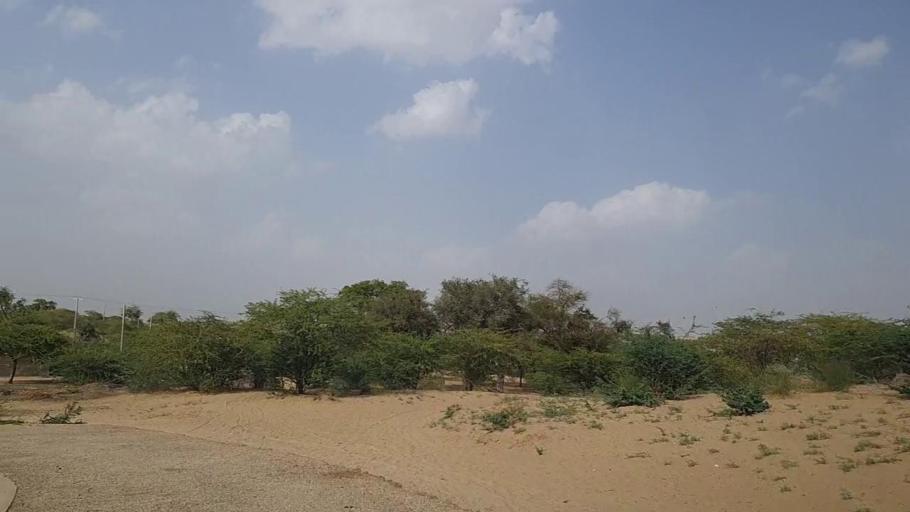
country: PK
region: Sindh
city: Islamkot
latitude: 24.8767
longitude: 70.1718
